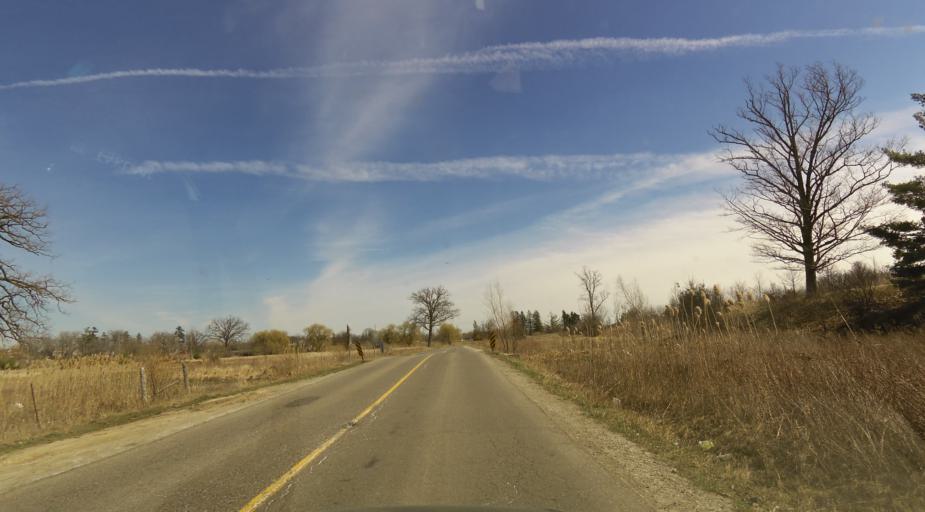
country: CA
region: Ontario
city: Brampton
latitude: 43.6401
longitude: -79.7694
